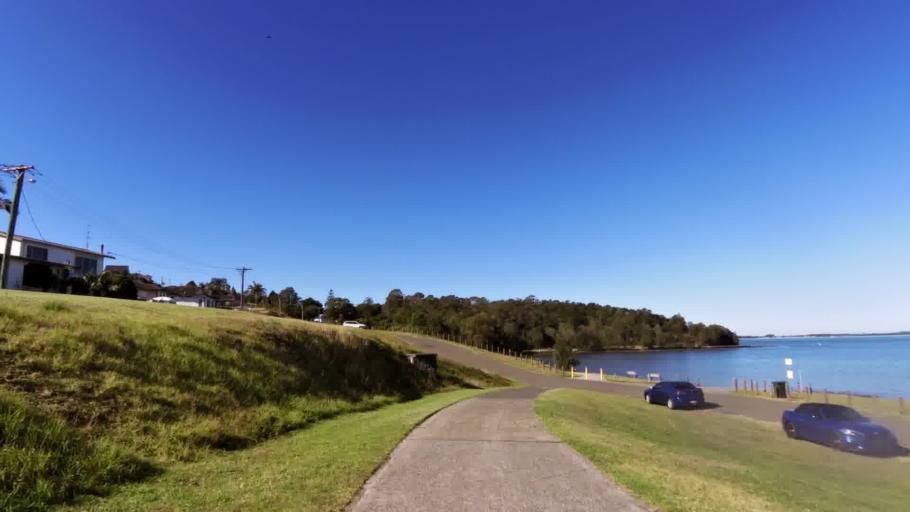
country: AU
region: New South Wales
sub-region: Wollongong
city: Berkeley
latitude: -34.4842
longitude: 150.8572
